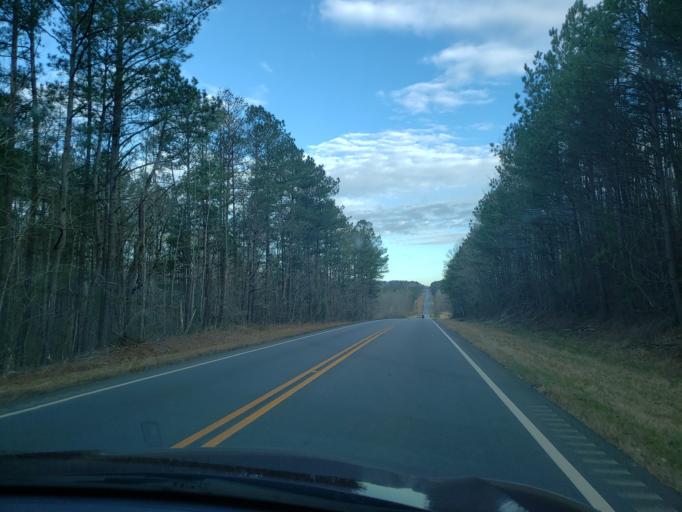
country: US
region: Alabama
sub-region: Randolph County
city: Wedowee
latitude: 33.2349
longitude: -85.4390
